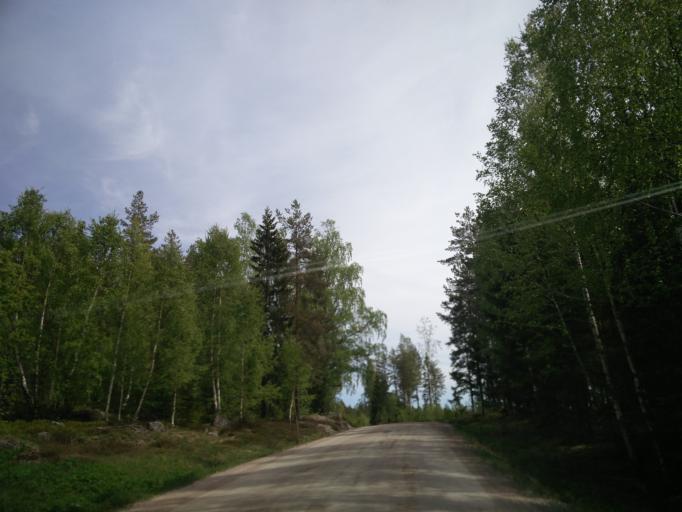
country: SE
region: Gaevleborg
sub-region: Hudiksvalls Kommun
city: Sorforsa
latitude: 61.7381
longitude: 16.9497
